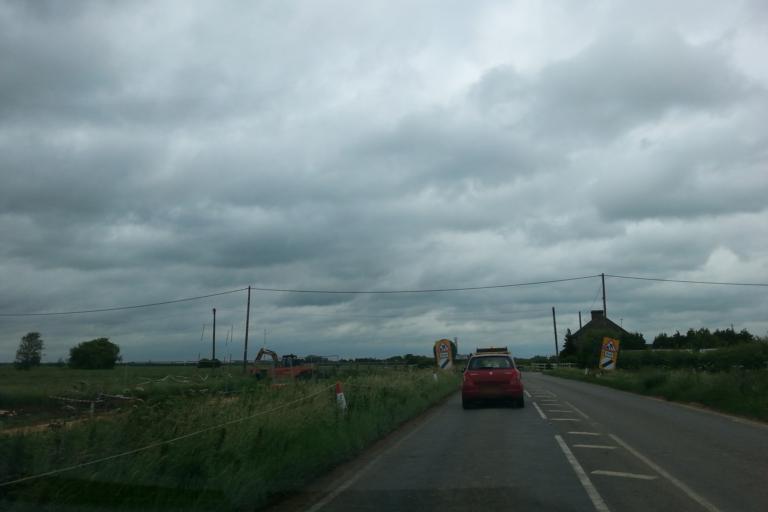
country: GB
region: England
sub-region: Cambridgeshire
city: Swavesey
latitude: 52.2615
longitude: 0.0278
